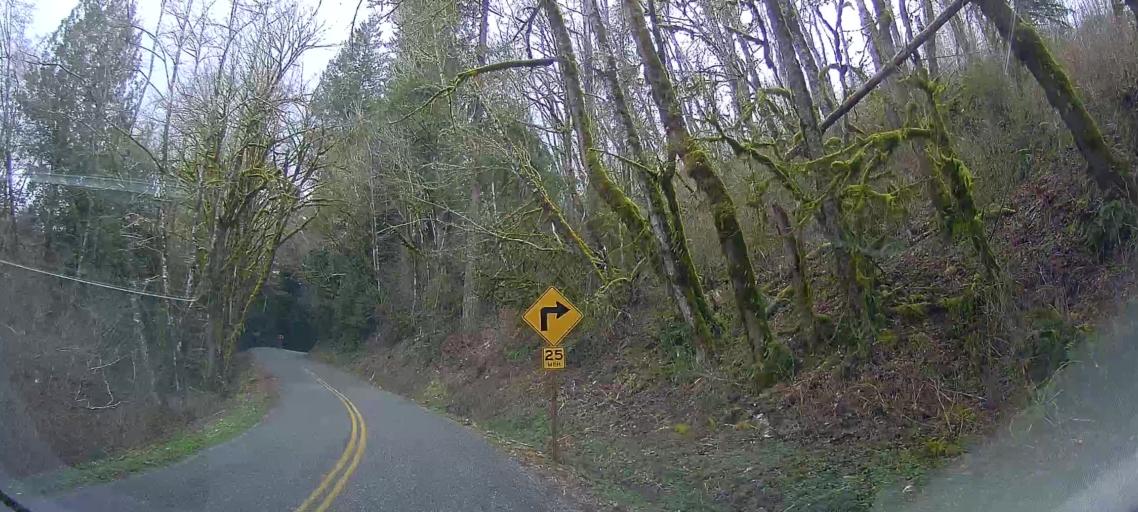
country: US
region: Washington
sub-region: Skagit County
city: Burlington
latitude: 48.5703
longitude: -122.3365
